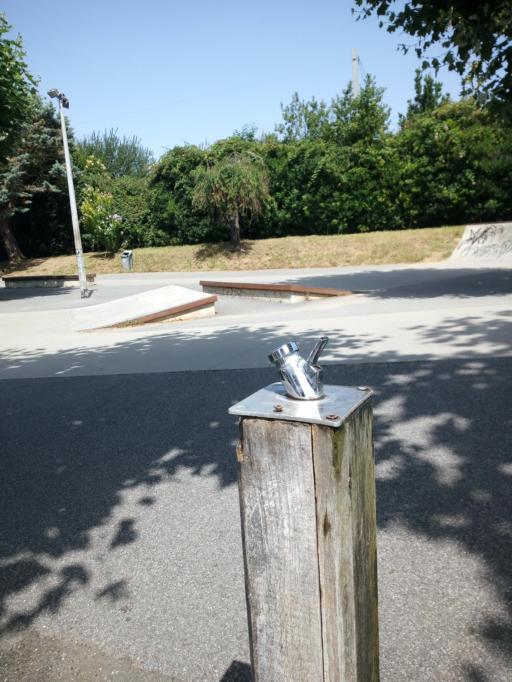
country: FR
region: Aquitaine
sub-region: Departement des Pyrenees-Atlantiques
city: Saint-Jean-de-Luz
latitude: 43.3857
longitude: -1.6596
